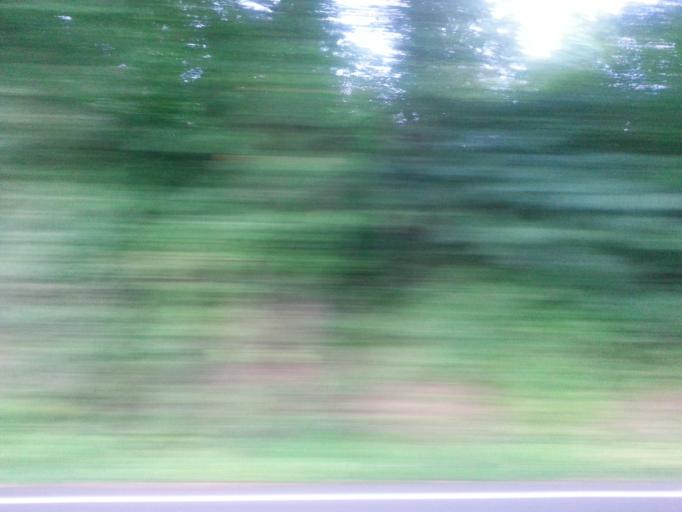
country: US
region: Tennessee
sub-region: Knox County
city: Knoxville
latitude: 36.0331
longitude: -83.9703
